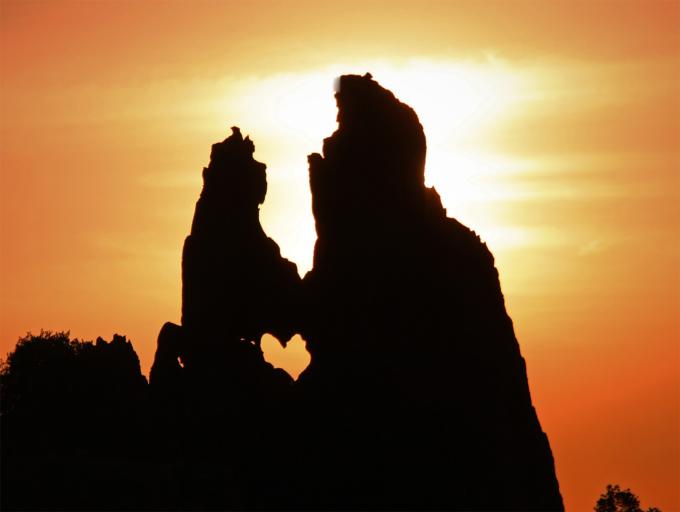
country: FR
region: Corsica
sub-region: Departement de la Corse-du-Sud
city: Cargese
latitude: 42.2449
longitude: 8.6538
